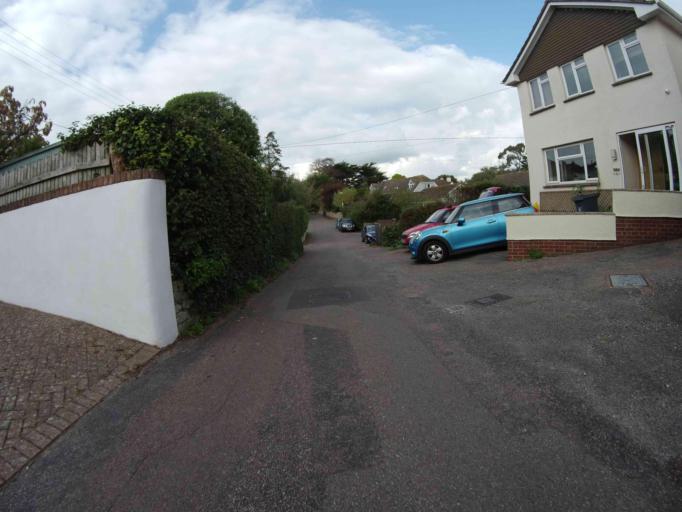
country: GB
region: England
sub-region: Devon
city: Budleigh Salterton
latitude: 50.6348
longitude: -3.3156
